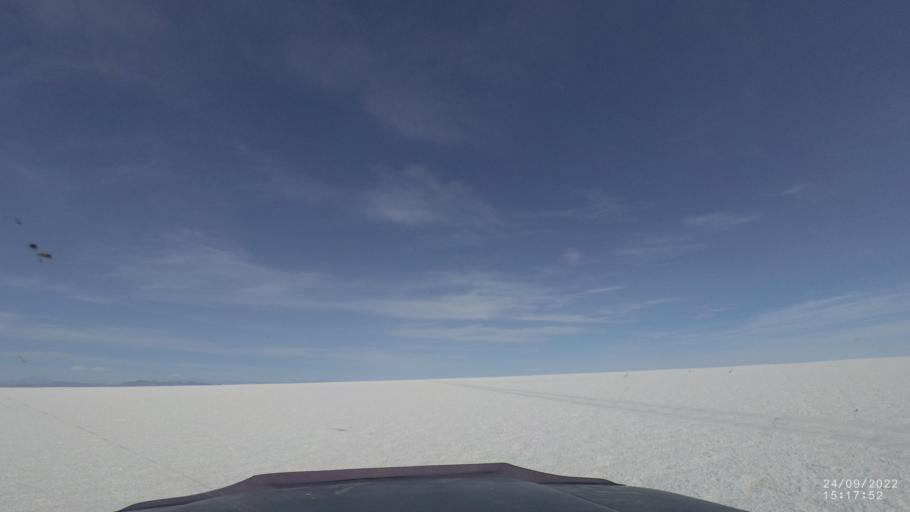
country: BO
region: Potosi
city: Colchani
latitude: -19.9929
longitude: -67.4232
